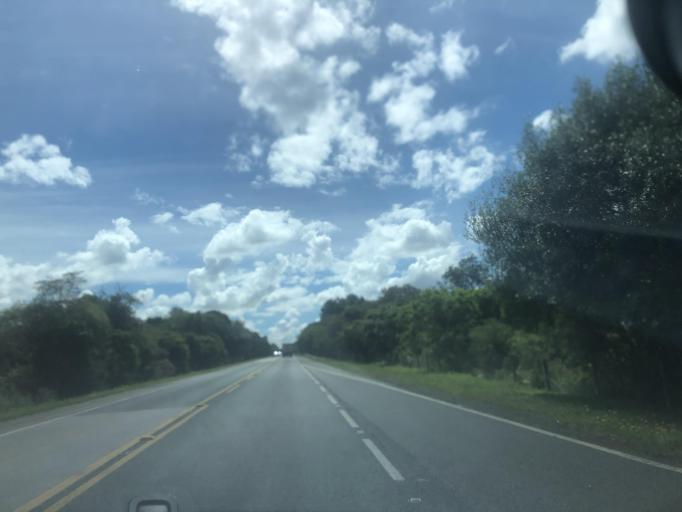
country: BR
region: Santa Catarina
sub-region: Tres Barras
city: Tres Barras
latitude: -26.3375
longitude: -50.0748
